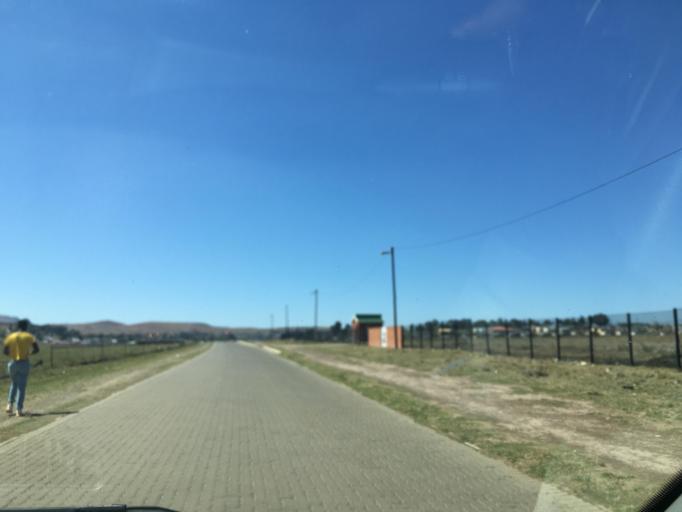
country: ZA
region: Eastern Cape
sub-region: Chris Hani District Municipality
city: Elliot
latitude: -31.3310
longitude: 27.8287
